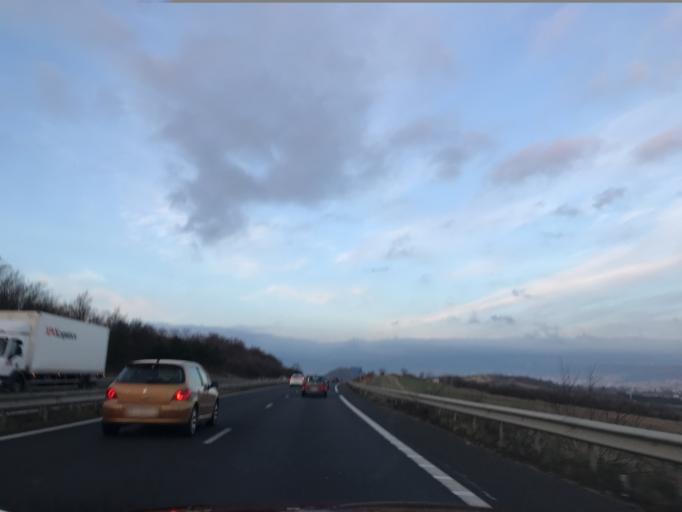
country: FR
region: Auvergne
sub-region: Departement du Puy-de-Dome
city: Aulnat
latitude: 45.7733
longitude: 3.1676
